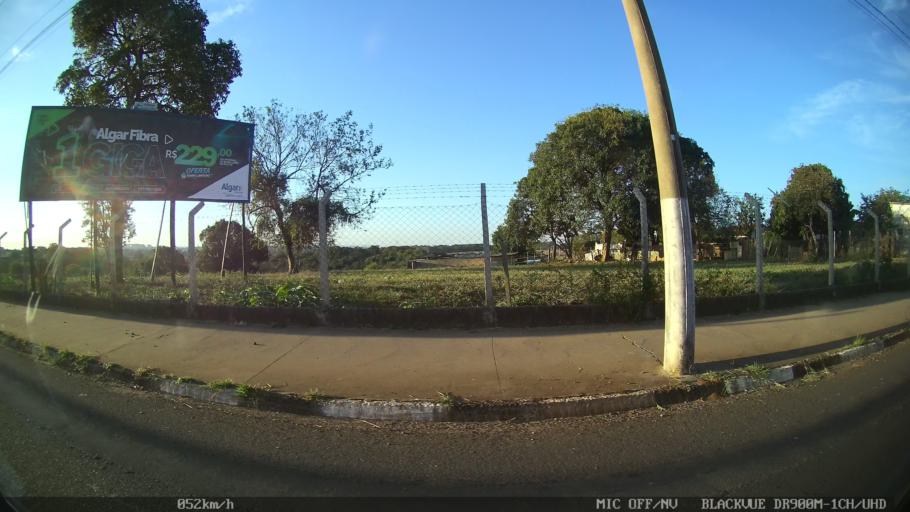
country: BR
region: Sao Paulo
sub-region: Franca
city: Franca
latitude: -20.5137
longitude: -47.3818
